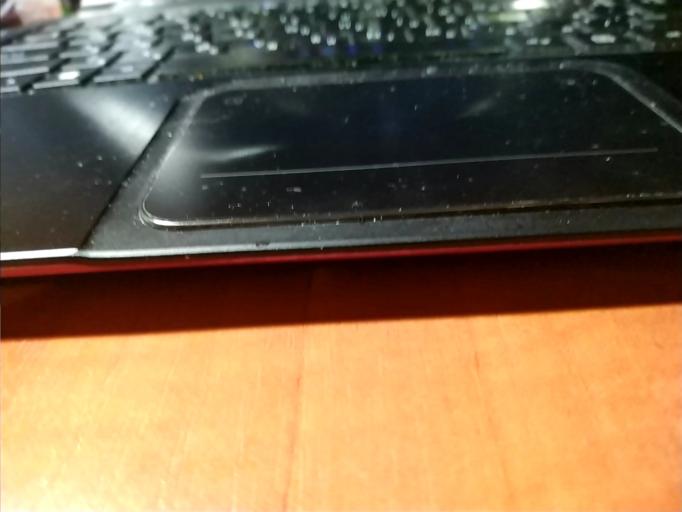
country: RU
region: Tverskaya
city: Ves'yegonsk
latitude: 58.6970
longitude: 37.5440
